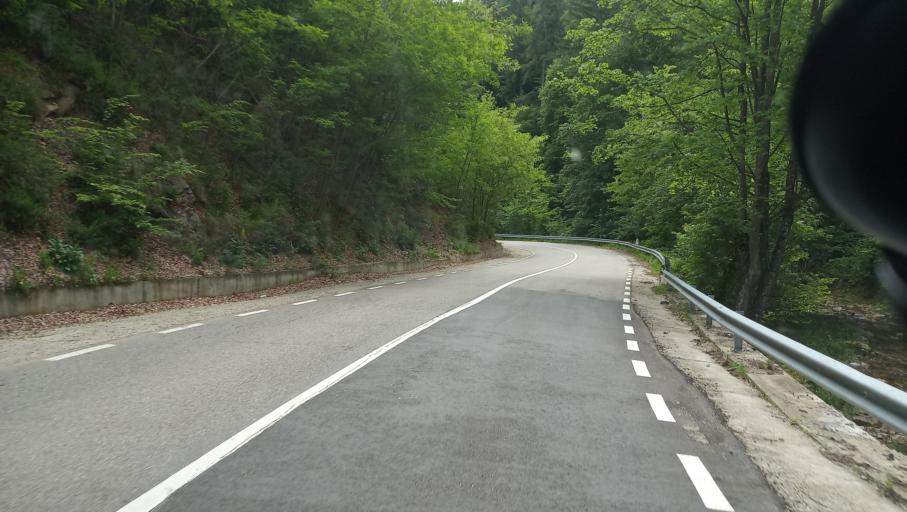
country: RO
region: Caras-Severin
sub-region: Comuna Bucosnita
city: Bucosnita
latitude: 45.2626
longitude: 22.2289
